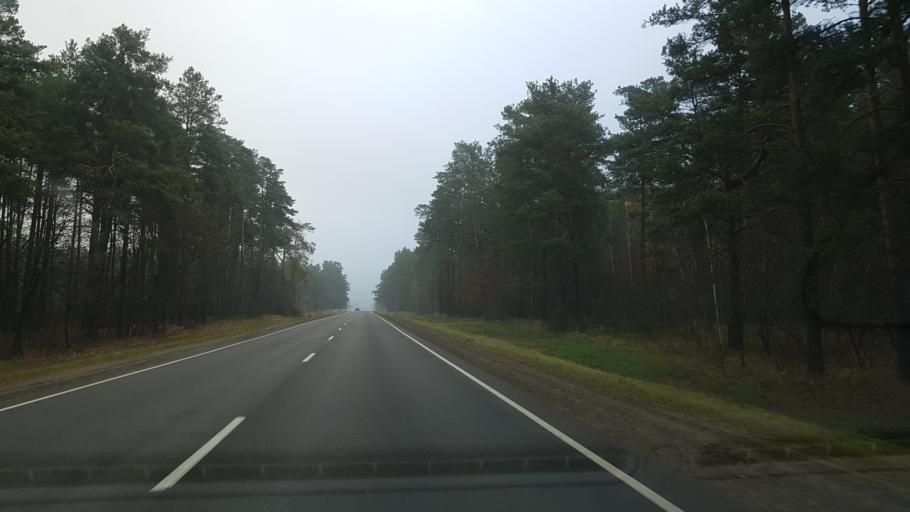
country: BY
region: Mogilev
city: Babruysk
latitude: 53.1643
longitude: 29.3278
